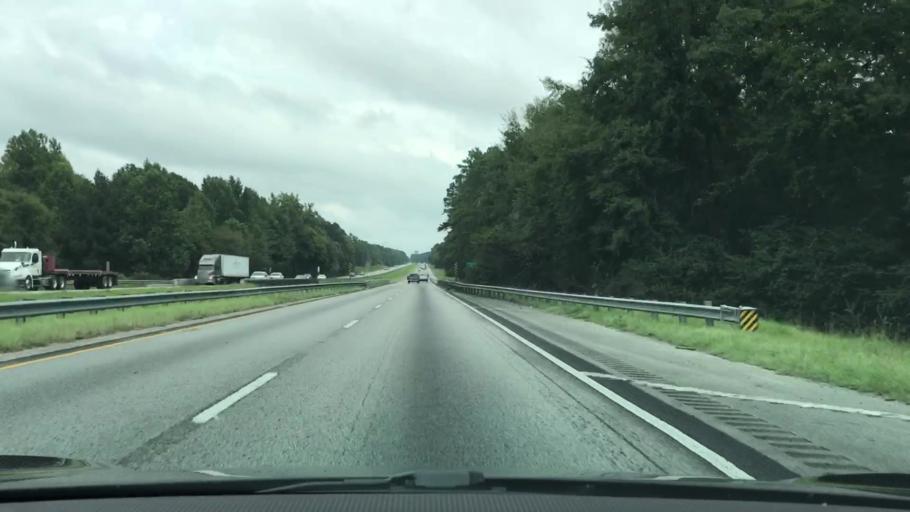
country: US
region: Alabama
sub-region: Lee County
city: Auburn
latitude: 32.5321
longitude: -85.5570
